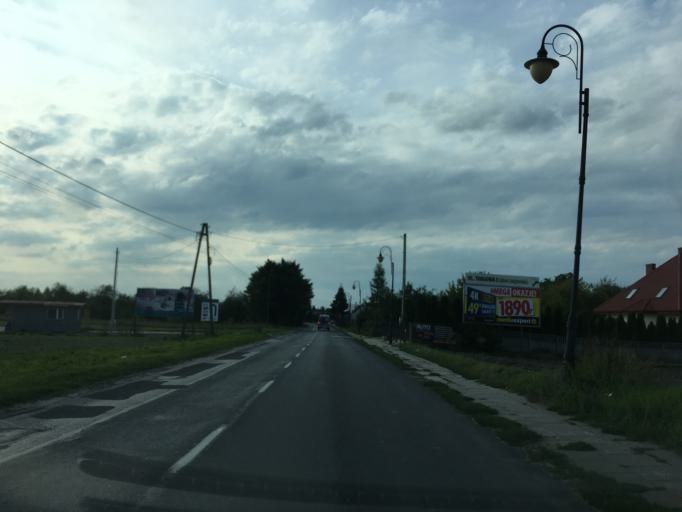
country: PL
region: Swietokrzyskie
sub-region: Powiat wloszczowski
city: Wloszczowa
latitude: 50.8471
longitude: 19.9948
